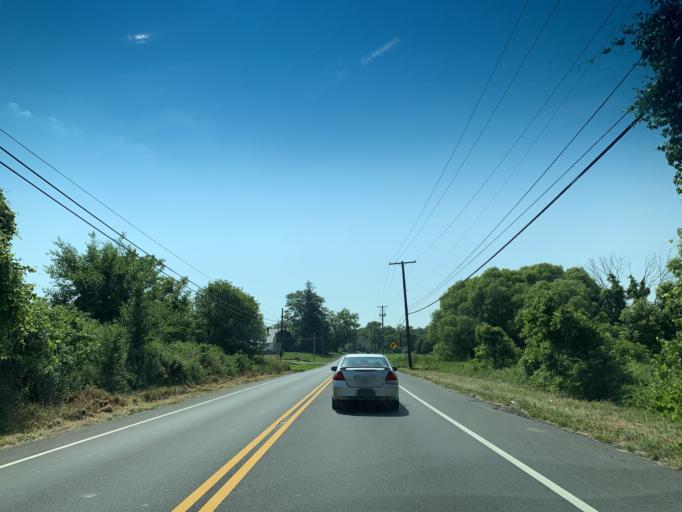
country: US
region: Maryland
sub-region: Montgomery County
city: Darnestown
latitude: 39.1284
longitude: -77.3403
